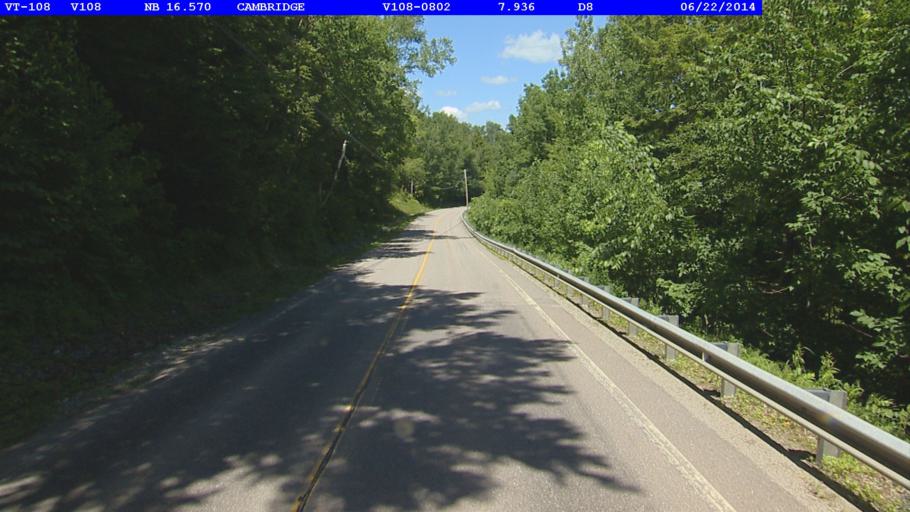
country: US
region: Vermont
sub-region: Lamoille County
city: Johnson
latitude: 44.6331
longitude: -72.8287
